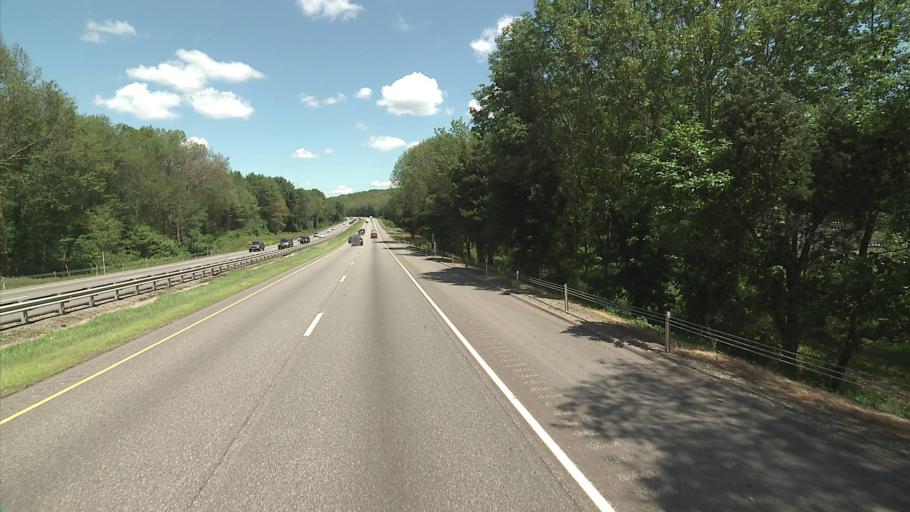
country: US
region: Connecticut
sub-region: New London County
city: Oxoboxo River
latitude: 41.4558
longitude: -72.1160
